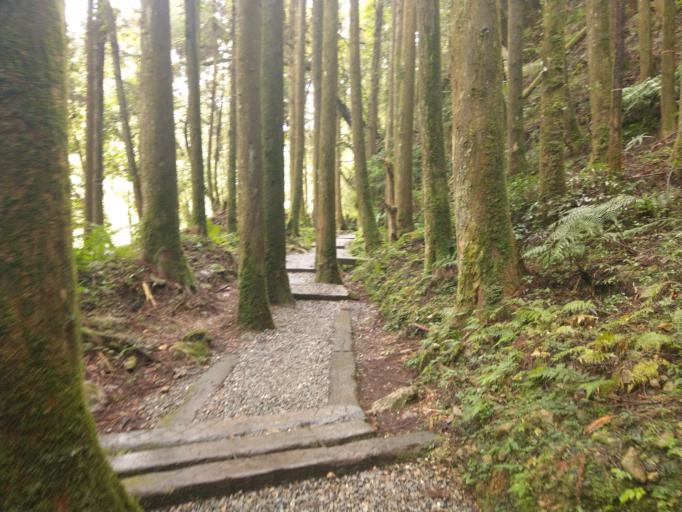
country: TW
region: Taiwan
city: Lugu
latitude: 23.6291
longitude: 120.7967
